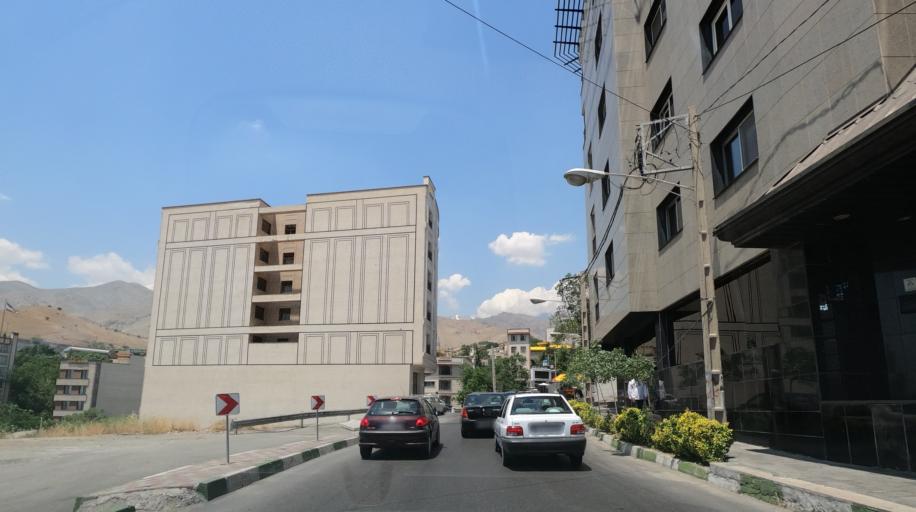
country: IR
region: Tehran
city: Tajrish
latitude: 35.7922
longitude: 51.3910
